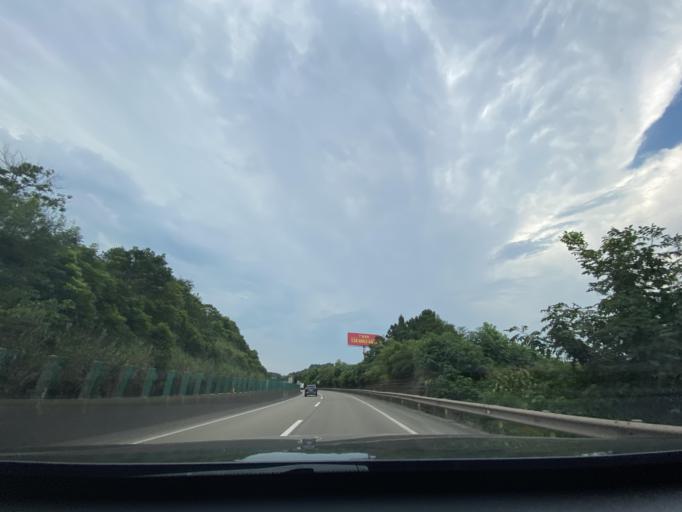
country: CN
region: Sichuan
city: Chonglong
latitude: 29.7123
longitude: 104.9411
